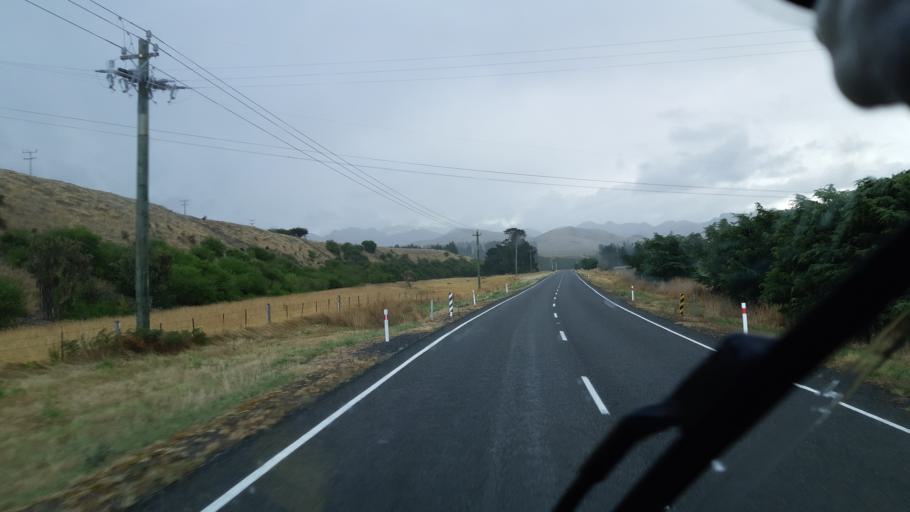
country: NZ
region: Canterbury
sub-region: Hurunui District
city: Amberley
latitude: -42.7003
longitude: 172.8076
